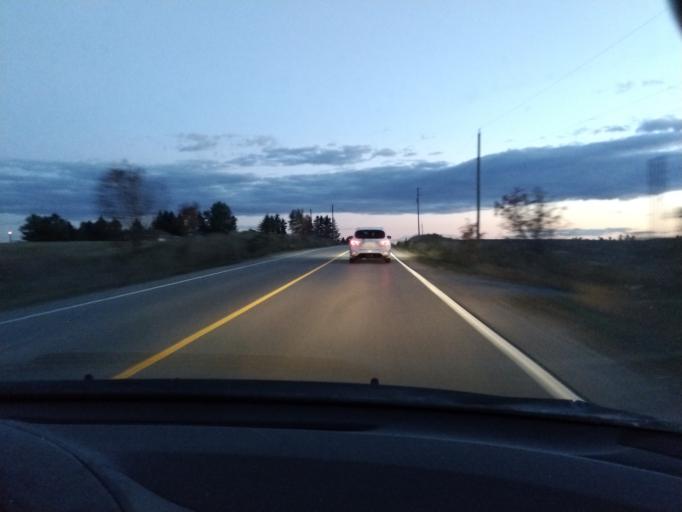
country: CA
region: Ontario
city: Bradford West Gwillimbury
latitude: 44.1183
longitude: -79.6441
